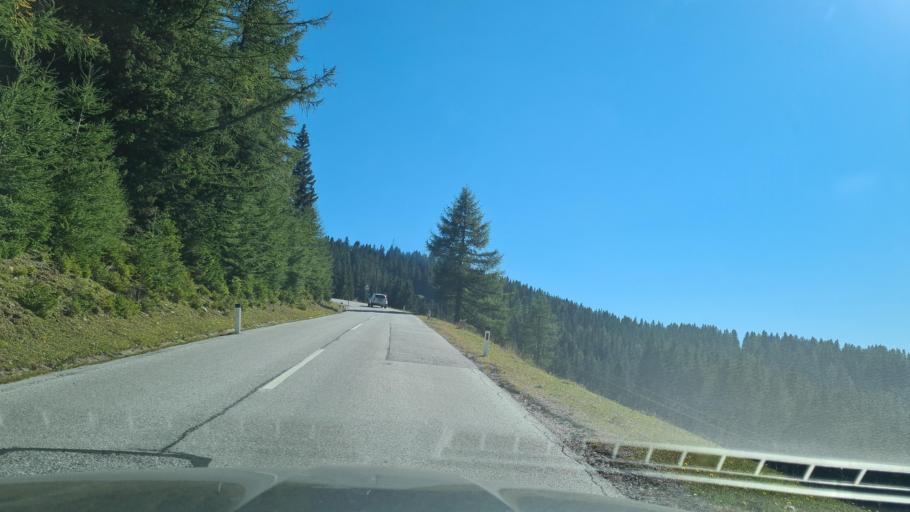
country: AT
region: Styria
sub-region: Politischer Bezirk Weiz
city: Gasen
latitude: 47.3482
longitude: 15.5497
